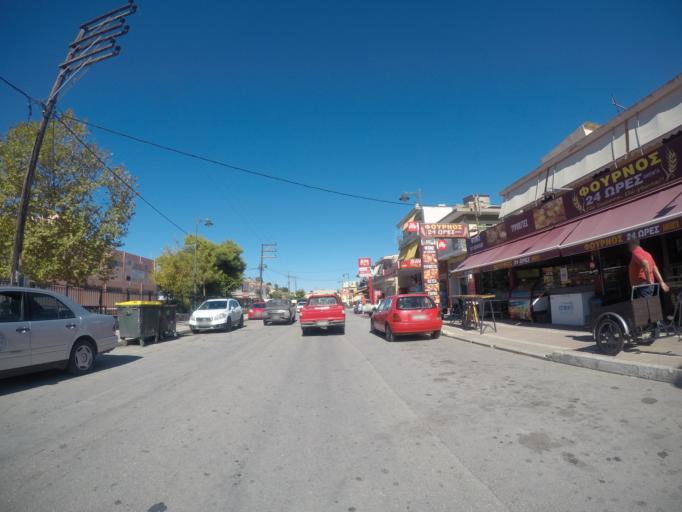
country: GR
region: West Greece
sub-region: Nomos Aitolias kai Akarnanias
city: Vonitsa
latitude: 38.9152
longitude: 20.8898
